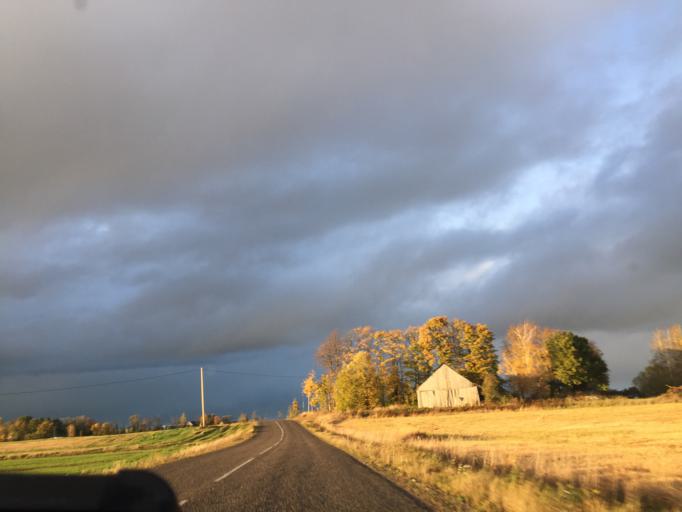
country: LV
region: Talsu Rajons
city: Sabile
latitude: 56.9340
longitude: 22.3972
